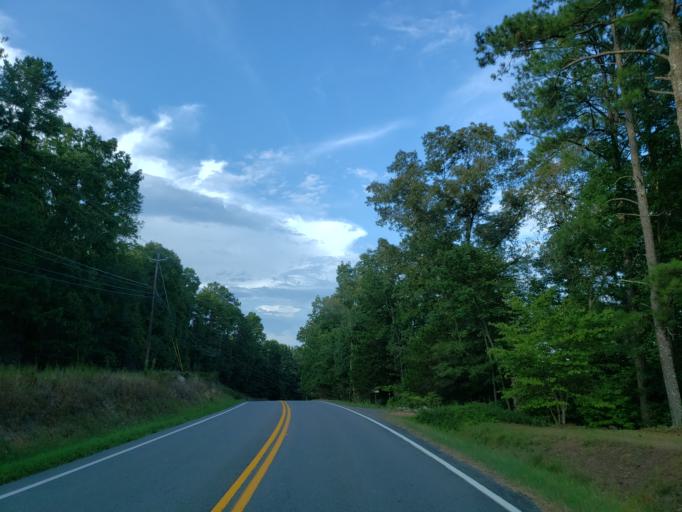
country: US
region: Georgia
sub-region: Bartow County
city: Euharlee
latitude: 34.2435
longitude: -84.9196
